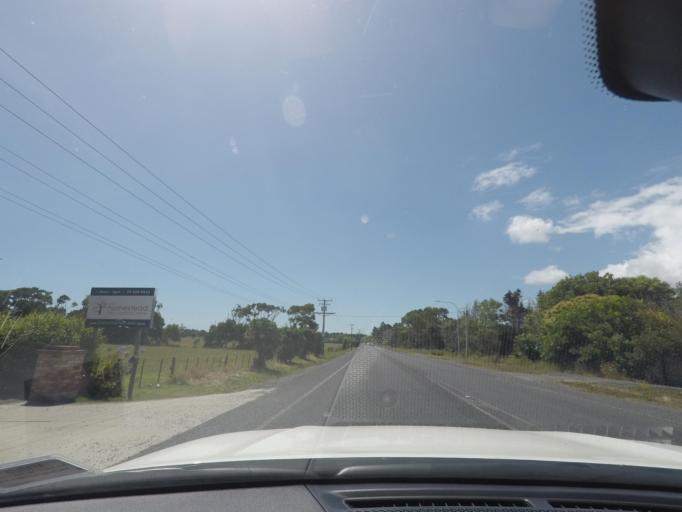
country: NZ
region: Auckland
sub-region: Auckland
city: Parakai
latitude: -36.6728
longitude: 174.4411
